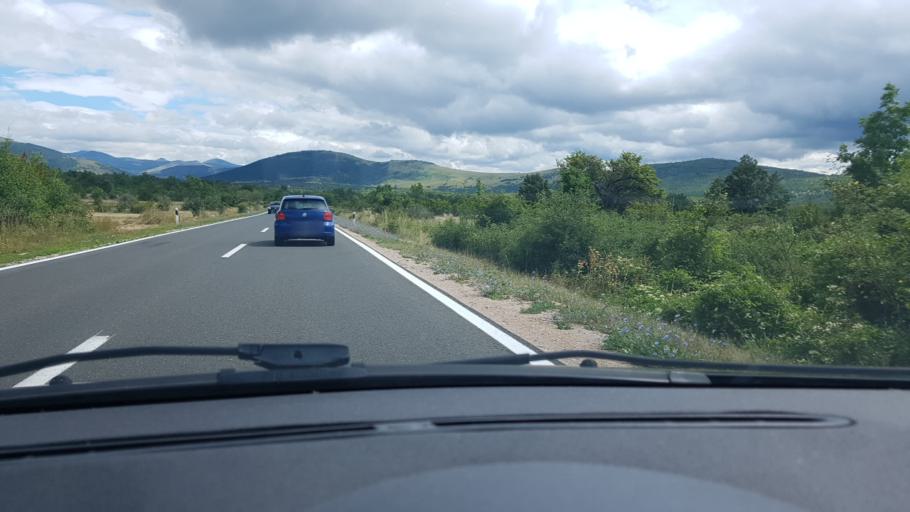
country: HR
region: Zadarska
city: Gracac
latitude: 44.4411
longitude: 15.8544
